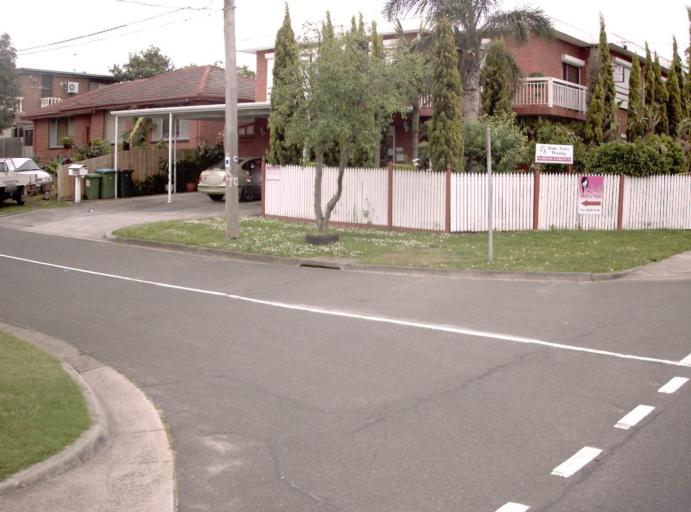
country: AU
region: Victoria
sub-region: Knox
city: Wantirna
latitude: -37.8316
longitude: 145.2272
